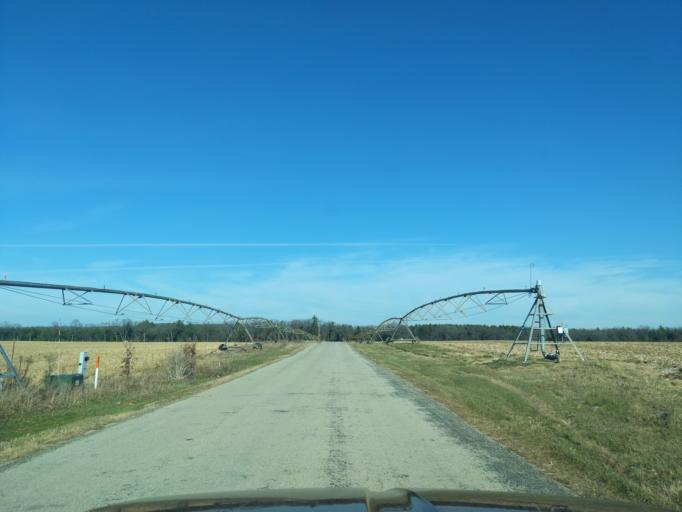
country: US
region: Wisconsin
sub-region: Waushara County
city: Silver Lake
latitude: 44.0939
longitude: -89.1739
